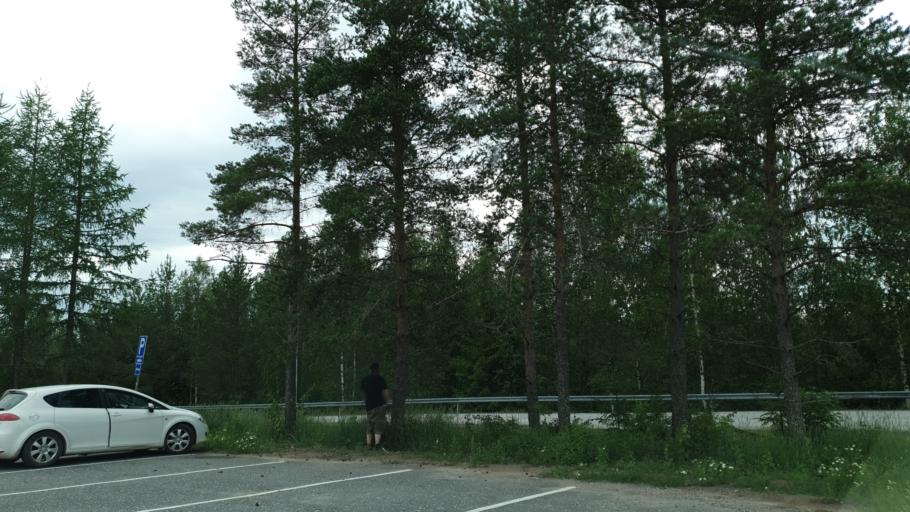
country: FI
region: Paijanne Tavastia
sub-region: Lahti
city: Hollola
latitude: 60.8281
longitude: 25.5283
